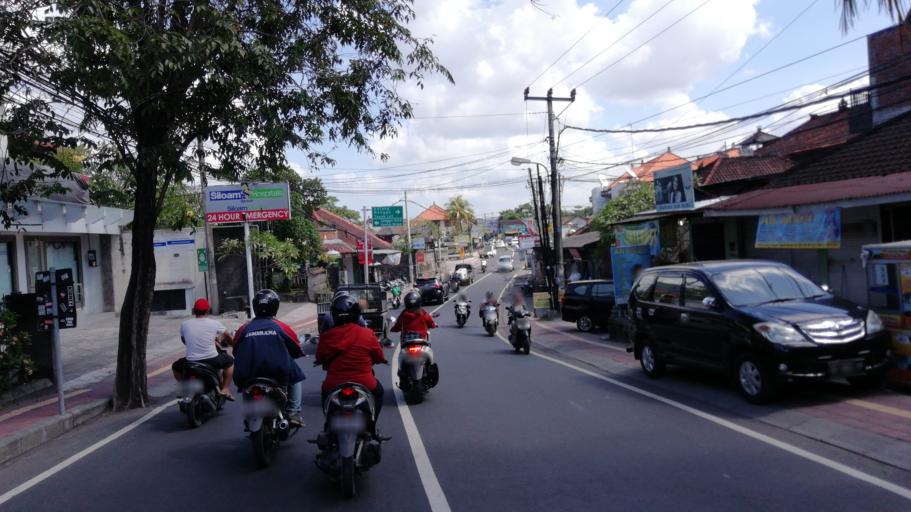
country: ID
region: Bali
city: Banjar Gunungpande
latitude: -8.6435
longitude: 115.1560
